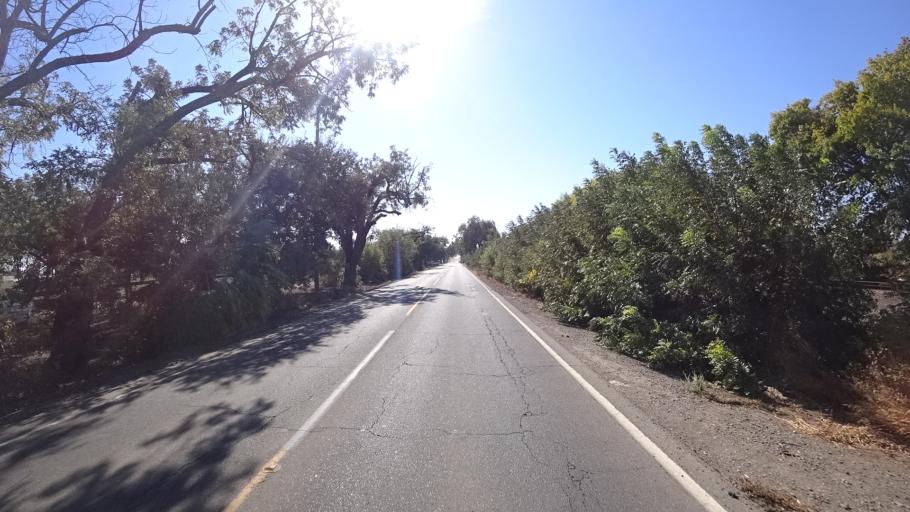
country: US
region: California
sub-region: Yolo County
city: Woodland
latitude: 38.6460
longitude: -121.7661
